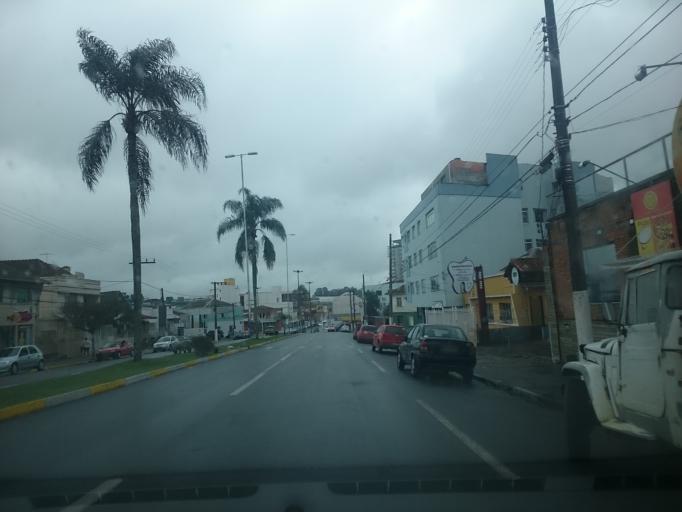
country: BR
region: Santa Catarina
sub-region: Lages
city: Lages
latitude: -27.8181
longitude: -50.3318
